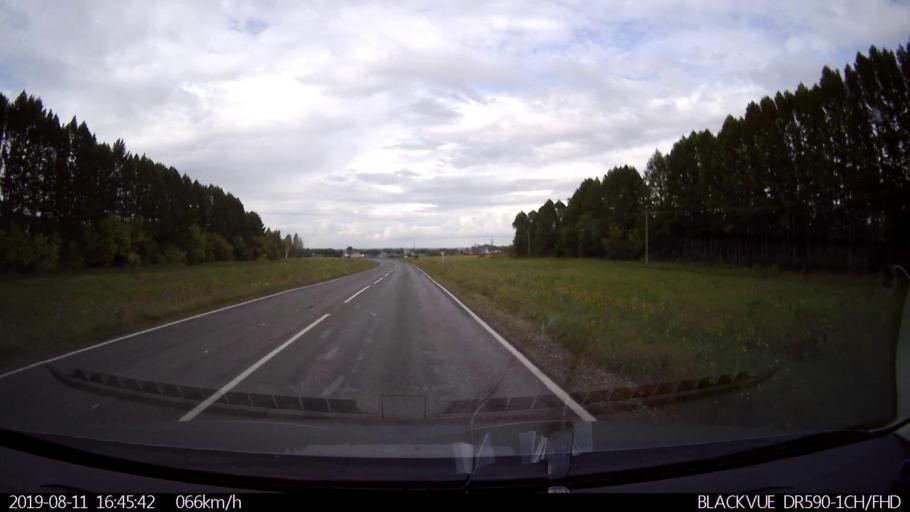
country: RU
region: Ulyanovsk
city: Mayna
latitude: 54.1924
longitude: 47.6876
